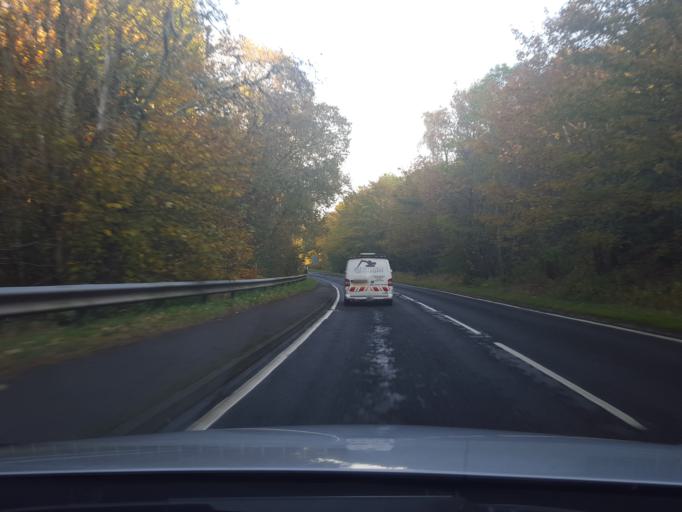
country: GB
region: Scotland
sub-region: Highland
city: Inverness
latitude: 57.4592
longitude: -4.2616
